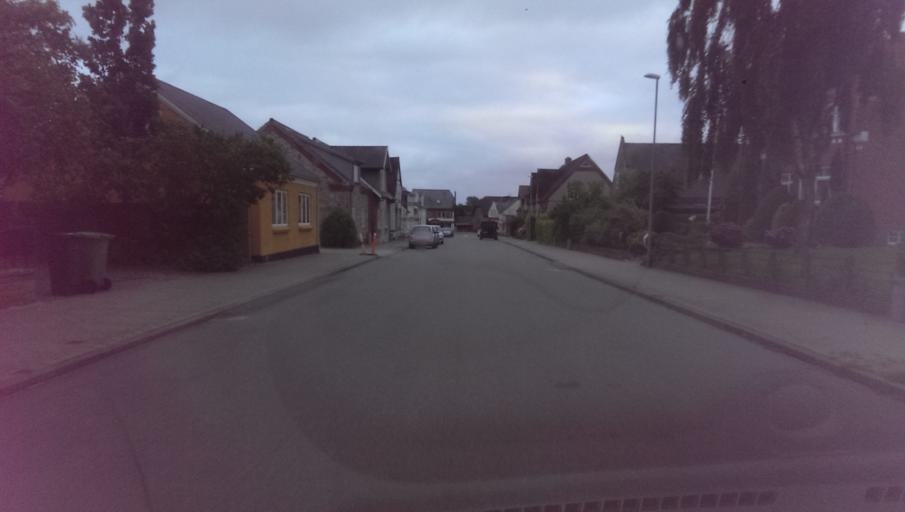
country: DK
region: South Denmark
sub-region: Esbjerg Kommune
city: Esbjerg
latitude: 55.4772
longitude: 8.4824
